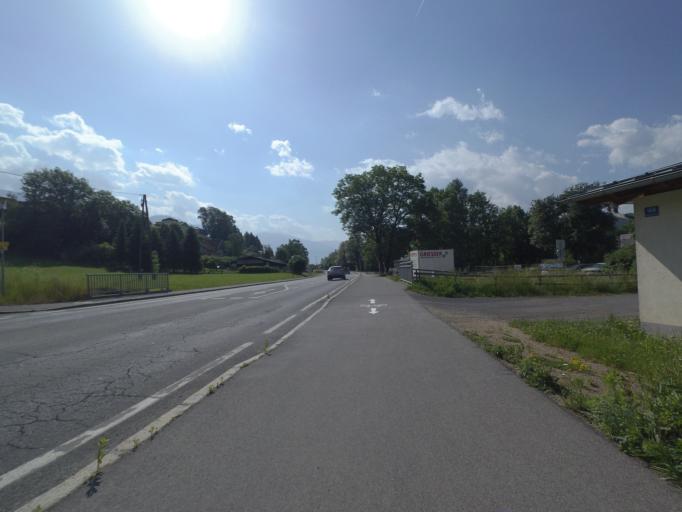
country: AT
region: Carinthia
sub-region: Politischer Bezirk Spittal an der Drau
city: Seeboden
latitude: 46.8172
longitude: 13.5292
